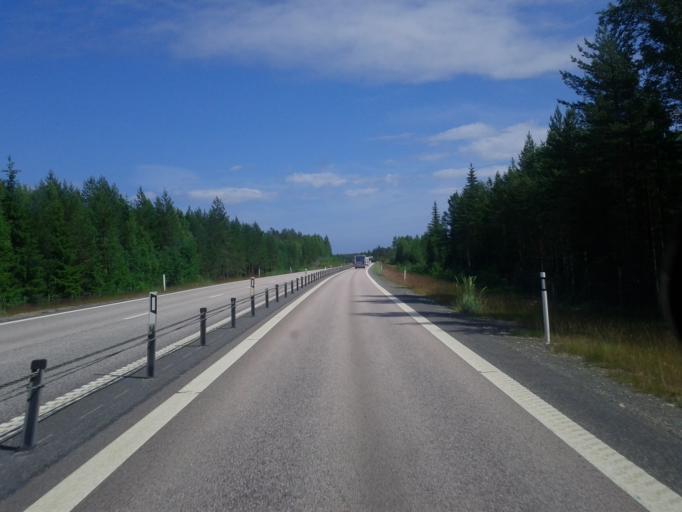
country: SE
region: Vaesternorrland
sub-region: OErnskoeldsviks Kommun
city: Husum
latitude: 63.4566
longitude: 19.2442
